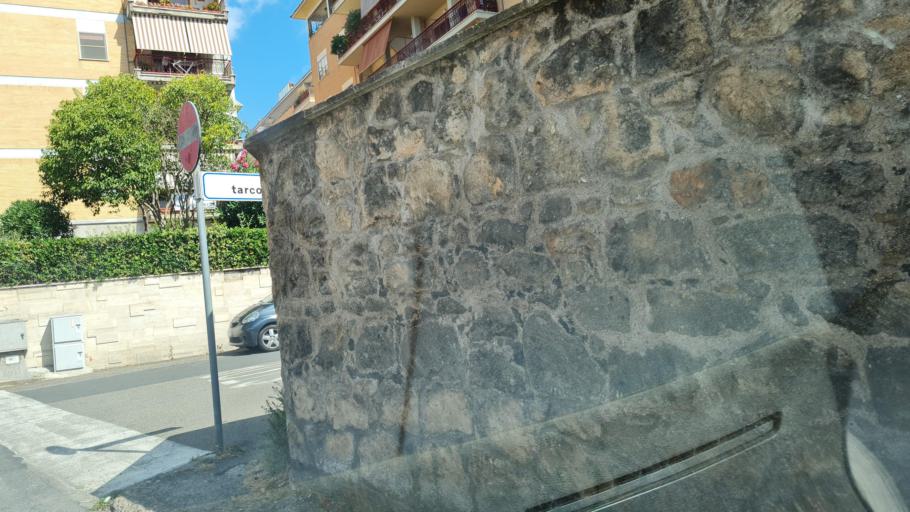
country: IT
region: Latium
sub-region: Provincia di Viterbo
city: Tarquinia
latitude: 42.2503
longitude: 11.7576
